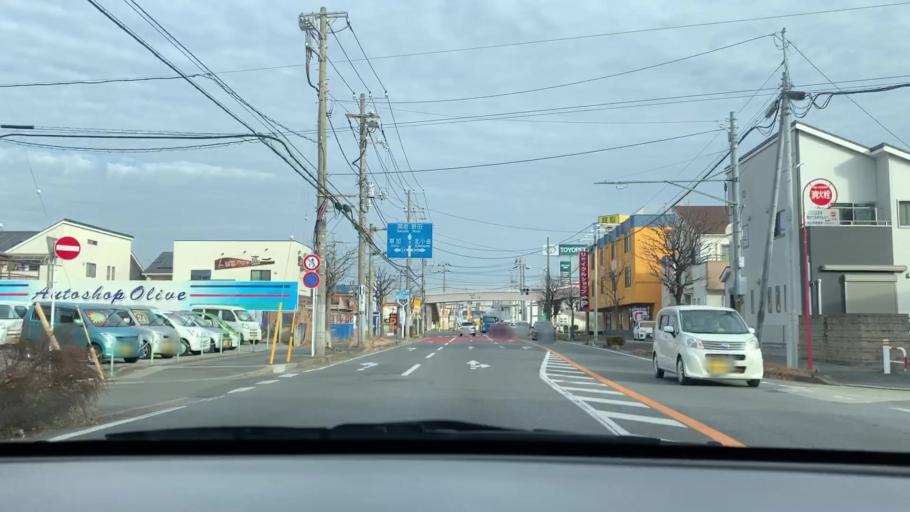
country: JP
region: Chiba
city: Nagareyama
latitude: 35.8434
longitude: 139.8976
